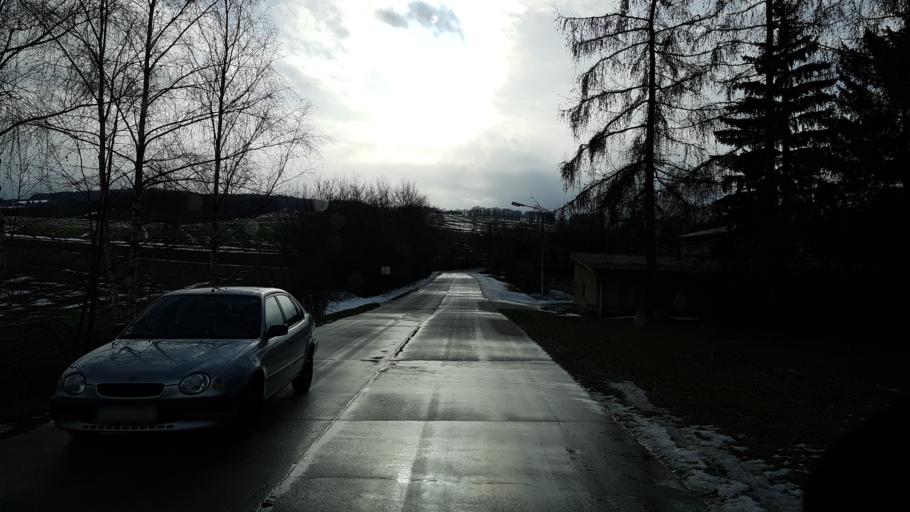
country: DE
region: Saxony
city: Wildenfels
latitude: 50.6458
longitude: 12.5686
